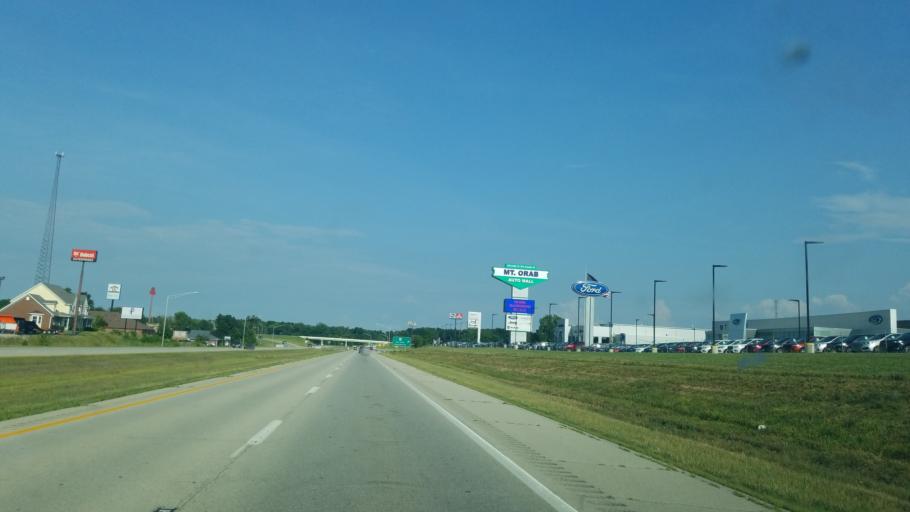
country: US
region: Ohio
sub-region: Brown County
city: Mount Orab
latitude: 39.0435
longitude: -83.9284
